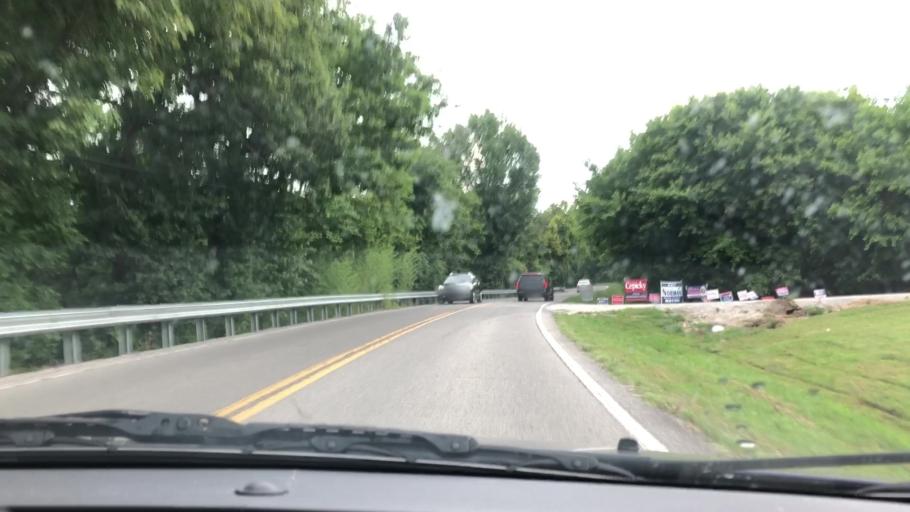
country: US
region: Tennessee
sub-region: Maury County
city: Columbia
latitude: 35.6796
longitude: -87.0129
